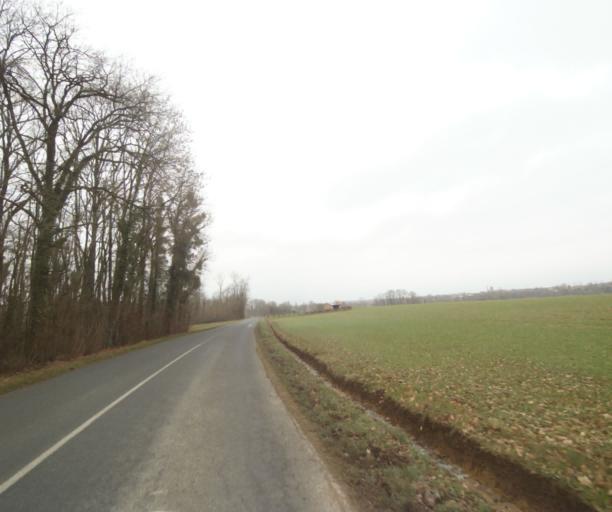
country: FR
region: Champagne-Ardenne
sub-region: Departement de la Marne
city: Pargny-sur-Saulx
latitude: 48.7382
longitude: 4.8571
